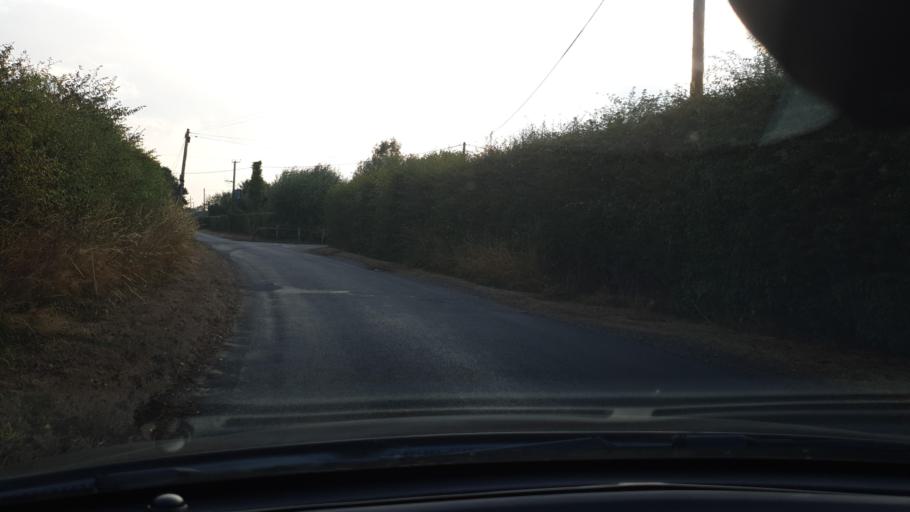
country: GB
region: England
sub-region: Essex
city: Alresford
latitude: 51.9089
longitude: 1.0099
